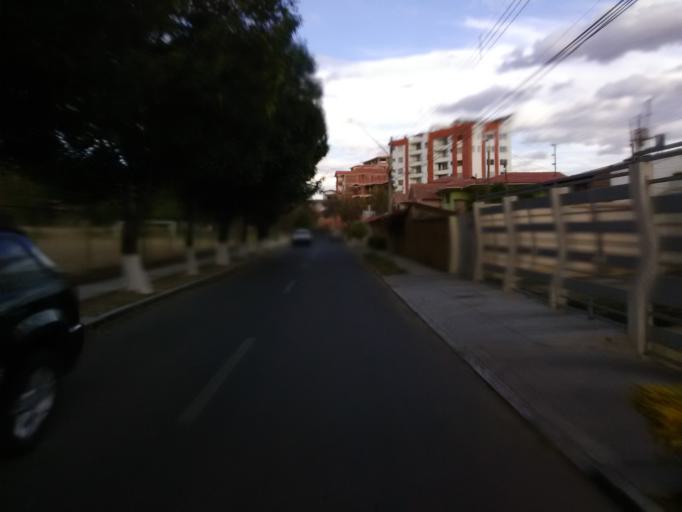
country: BO
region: Cochabamba
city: Cochabamba
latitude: -17.3667
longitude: -66.1733
